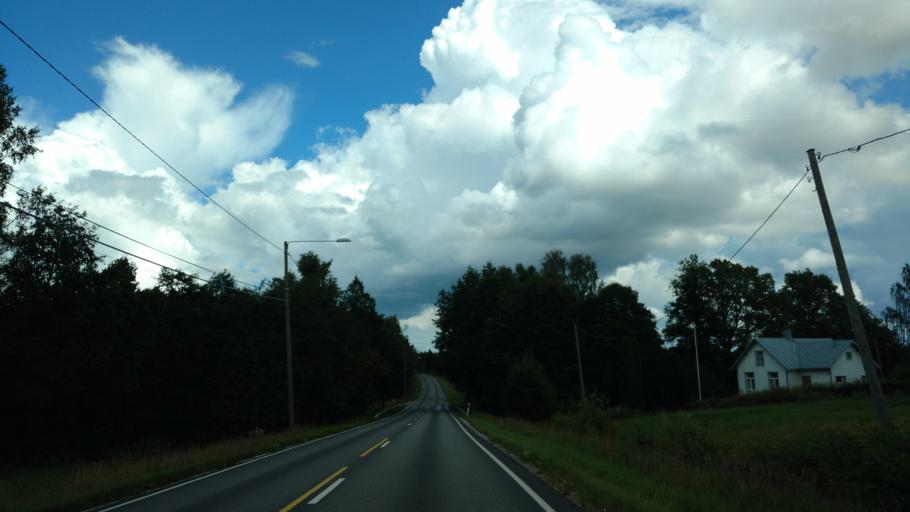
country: FI
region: Uusimaa
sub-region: Helsinki
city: Karjalohja
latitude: 60.2225
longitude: 23.6901
